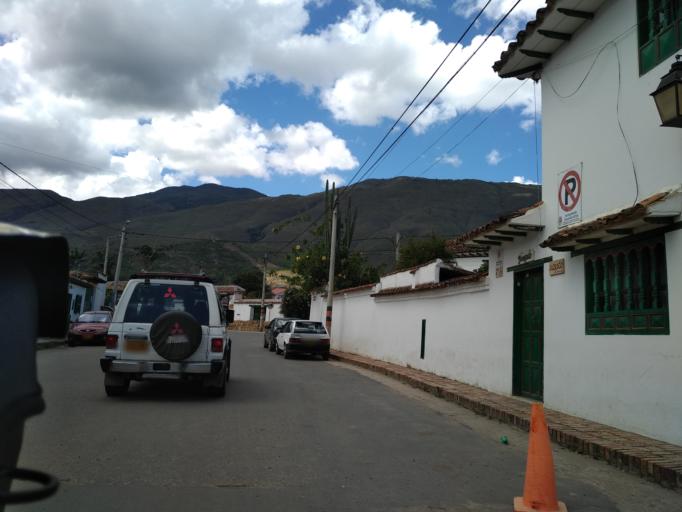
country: CO
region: Boyaca
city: Villa de Leiva
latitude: 5.6325
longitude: -73.5265
